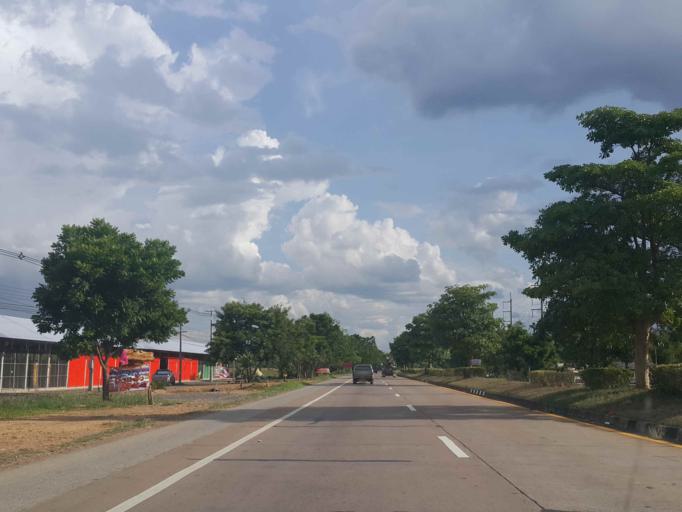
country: TH
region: Phrae
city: Sung Men
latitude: 18.0181
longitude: 100.1086
